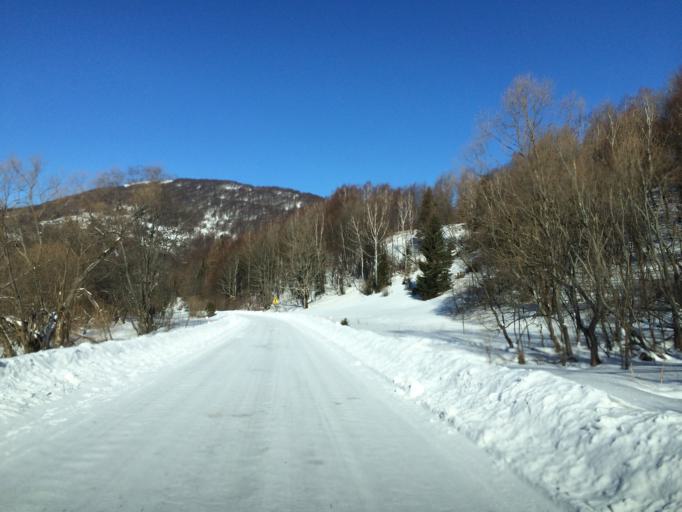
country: PL
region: Subcarpathian Voivodeship
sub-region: Powiat bieszczadzki
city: Lutowiska
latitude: 49.1370
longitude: 22.5726
